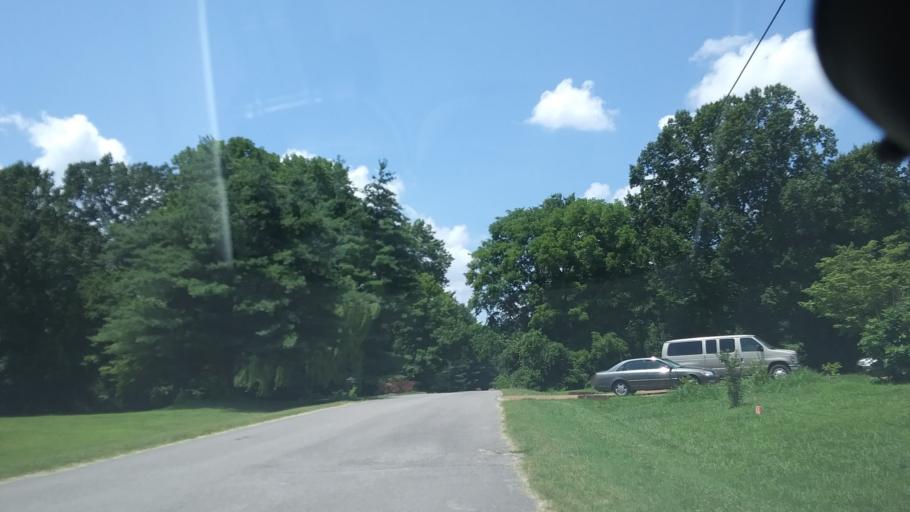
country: US
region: Tennessee
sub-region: Davidson County
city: Belle Meade
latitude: 36.0875
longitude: -86.9483
